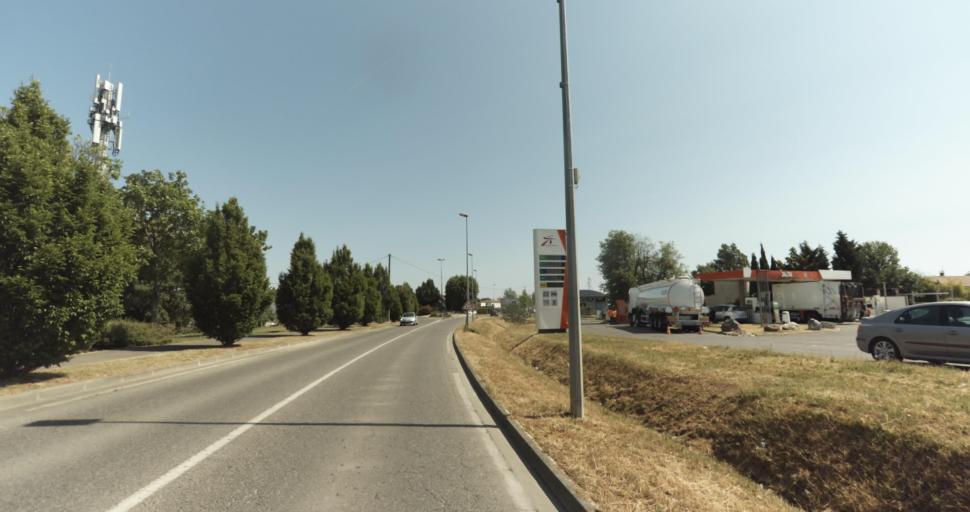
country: FR
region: Midi-Pyrenees
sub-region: Departement de la Haute-Garonne
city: La Salvetat-Saint-Gilles
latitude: 43.5812
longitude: 1.2736
